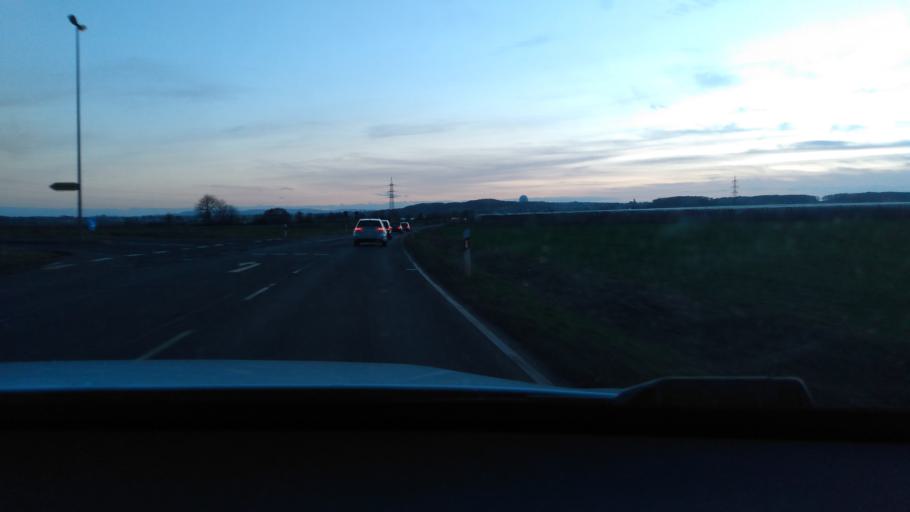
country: DE
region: North Rhine-Westphalia
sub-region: Regierungsbezirk Koln
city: Konigswinter
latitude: 50.6460
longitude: 7.1549
